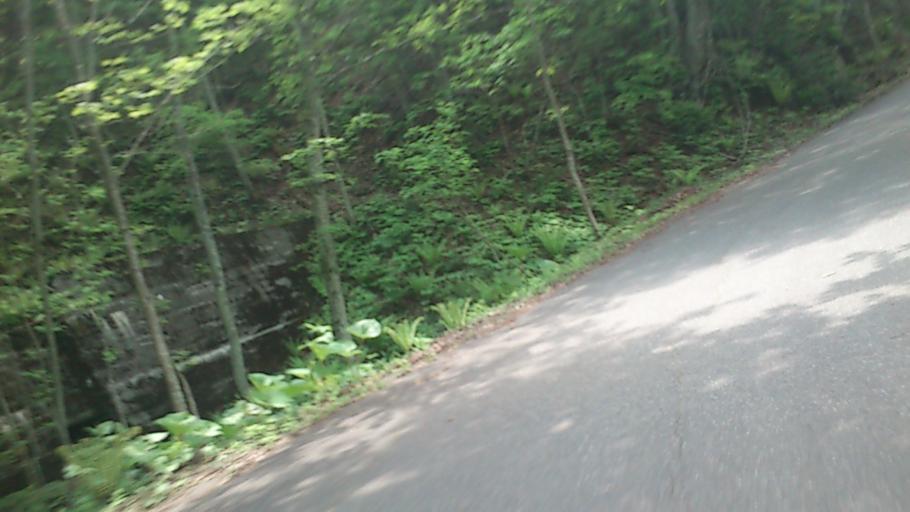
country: JP
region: Hokkaido
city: Otofuke
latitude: 43.3726
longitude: 143.2182
